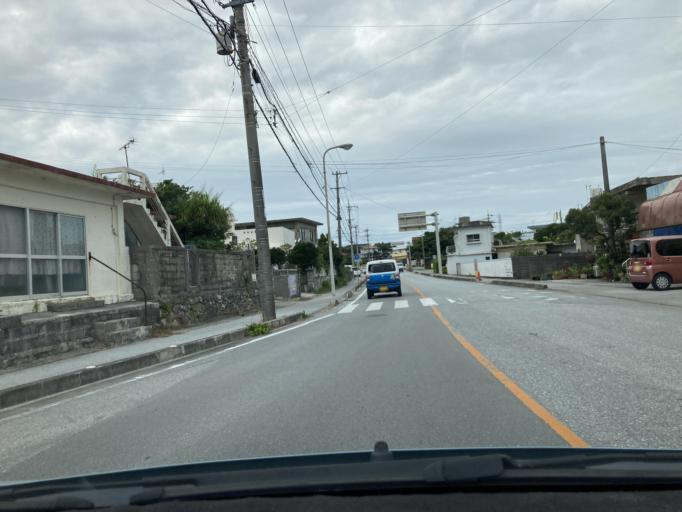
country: JP
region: Okinawa
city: Tomigusuku
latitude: 26.1556
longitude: 127.7806
